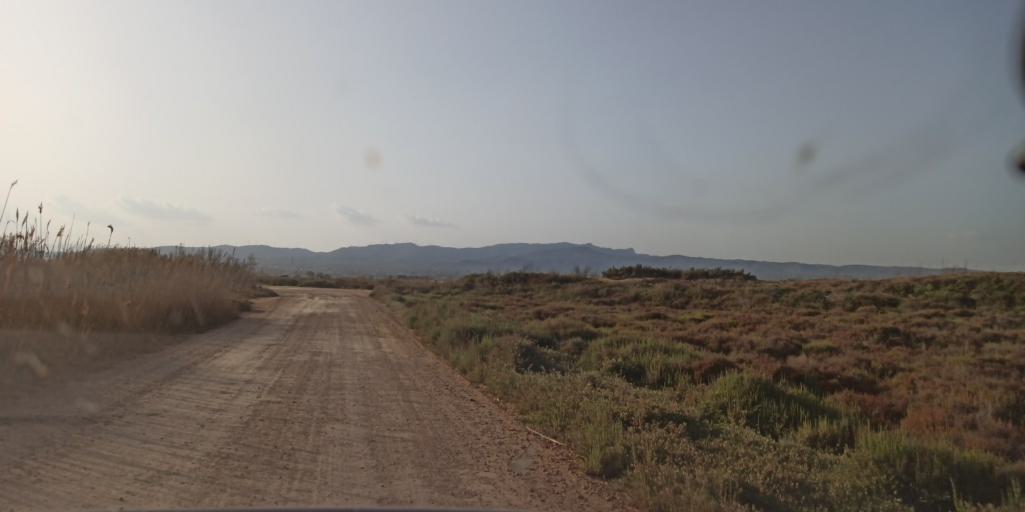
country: ES
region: Catalonia
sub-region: Provincia de Tarragona
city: L'Ampolla
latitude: 40.7780
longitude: 0.7212
